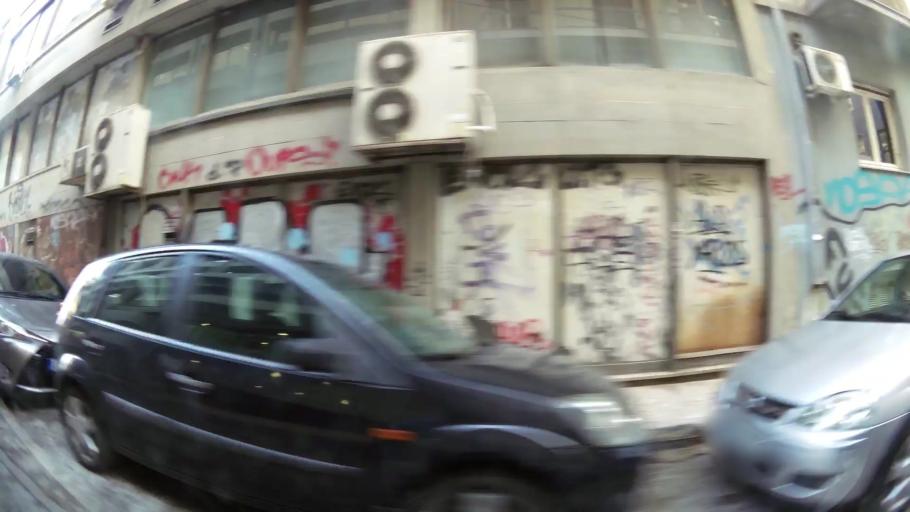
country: GR
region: Attica
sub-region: Nomarchia Athinas
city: Vyronas
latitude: 37.9765
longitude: 23.7545
